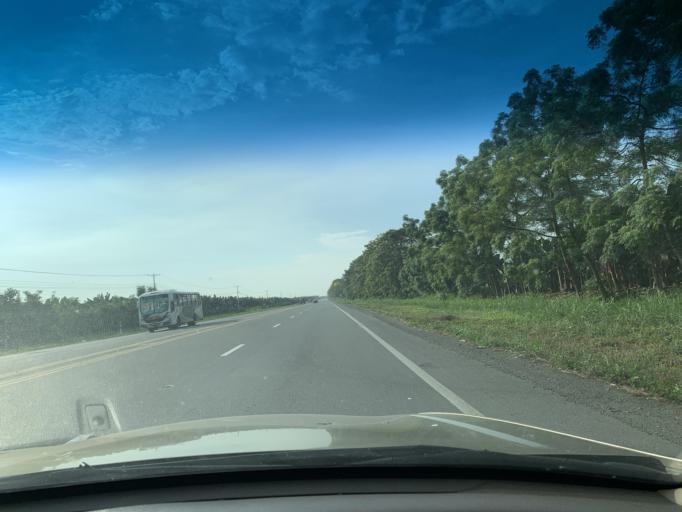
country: EC
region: Guayas
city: Coronel Marcelino Mariduena
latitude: -2.2787
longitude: -79.5315
